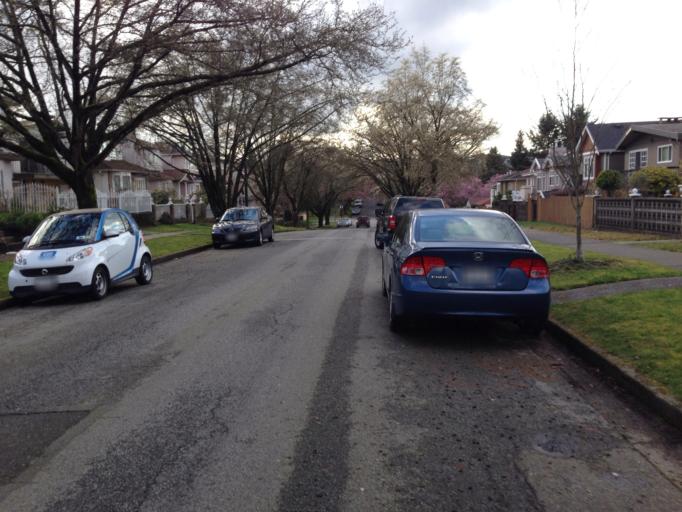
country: CA
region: British Columbia
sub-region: Fraser Valley Regional District
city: North Vancouver
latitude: 49.2704
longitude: -123.0347
